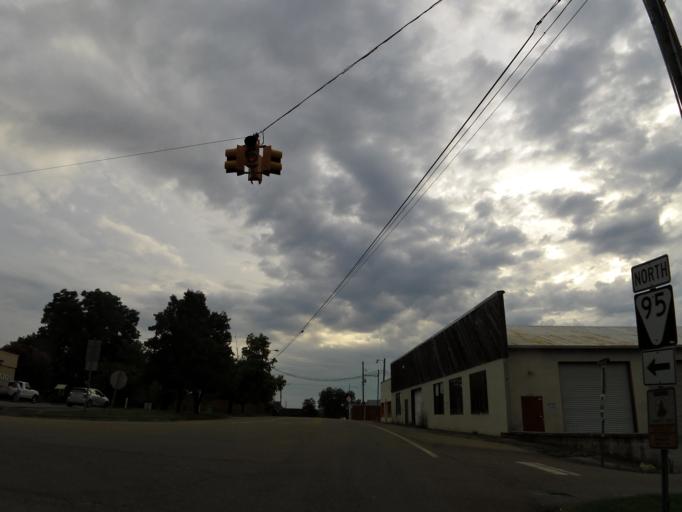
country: US
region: Tennessee
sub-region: Loudon County
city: Greenback
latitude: 35.6616
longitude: -84.1701
